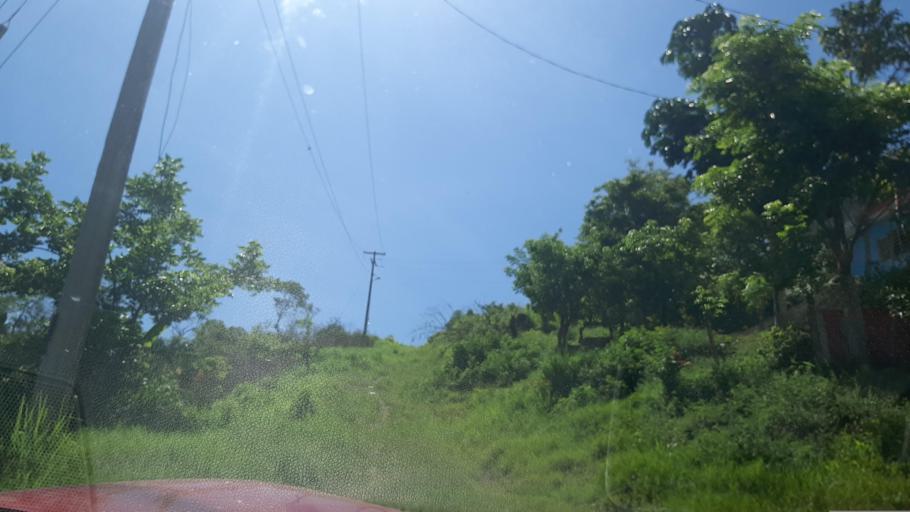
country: MX
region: Veracruz
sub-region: Poza Rica de Hidalgo
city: El Mollejon
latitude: 20.5553
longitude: -97.4182
